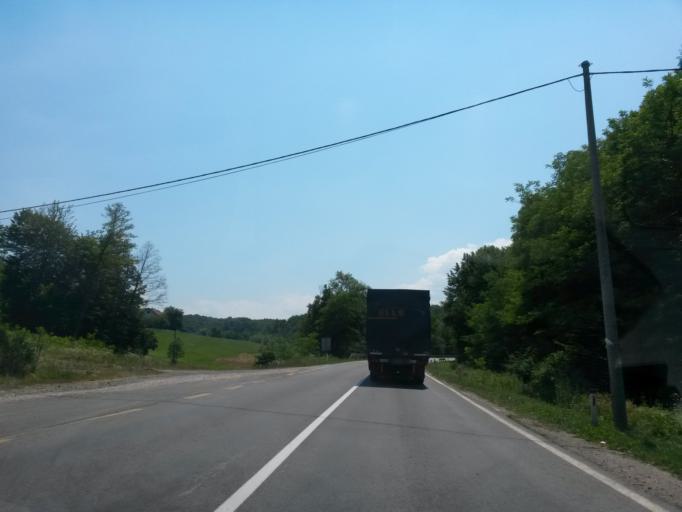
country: BA
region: Federation of Bosnia and Herzegovina
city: Lijesnica
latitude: 44.4626
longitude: 18.0655
